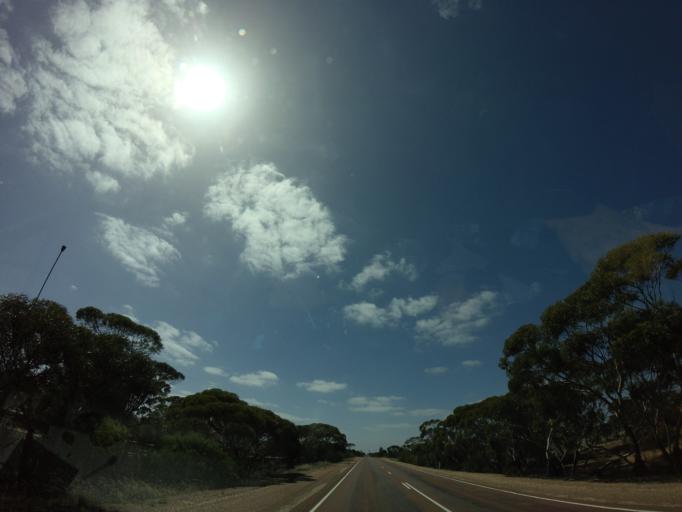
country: AU
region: South Australia
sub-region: Kimba
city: Caralue
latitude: -33.1180
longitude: 135.5383
